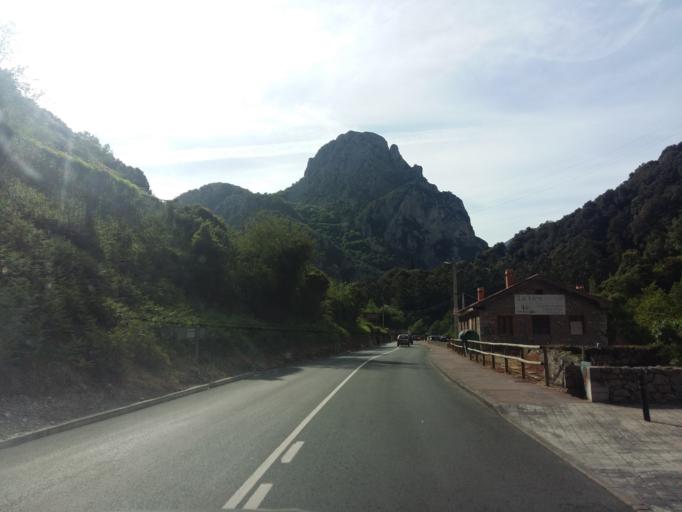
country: ES
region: Cantabria
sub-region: Provincia de Cantabria
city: Tresviso
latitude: 43.2517
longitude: -4.6072
